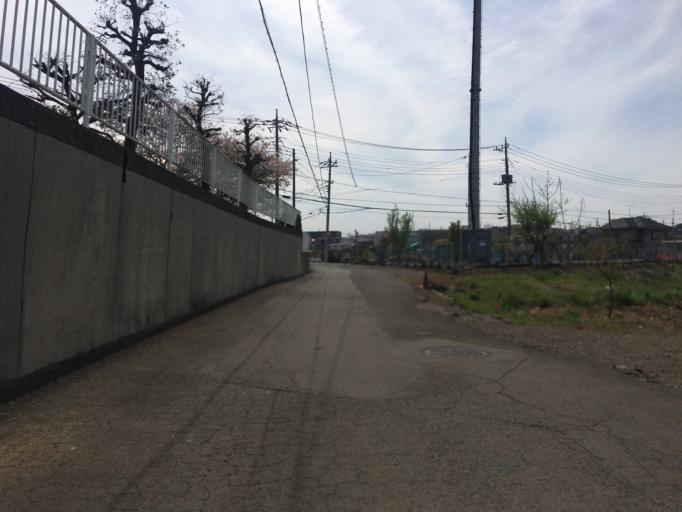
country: JP
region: Saitama
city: Shiki
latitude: 35.8482
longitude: 139.5552
